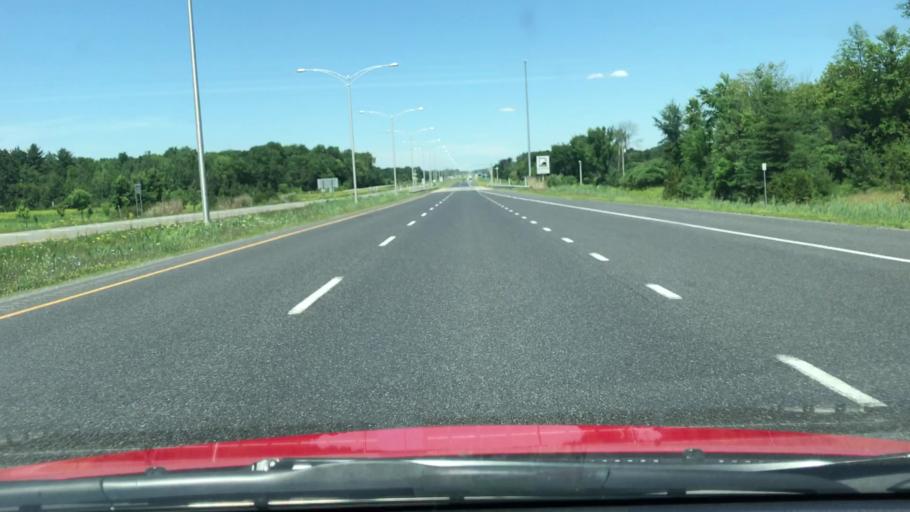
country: US
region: New York
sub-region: Clinton County
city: Champlain
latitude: 45.0208
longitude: -73.4529
